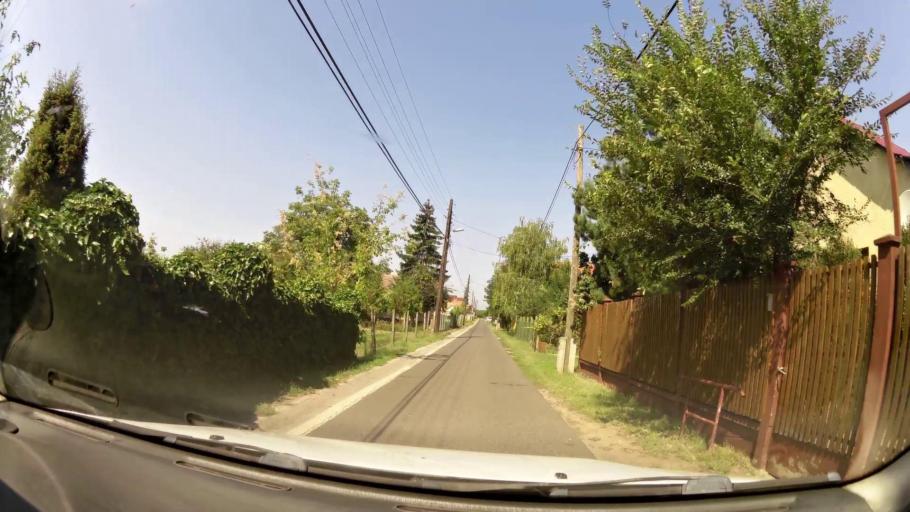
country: HU
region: Pest
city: Ujszilvas
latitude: 47.2711
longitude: 19.9092
